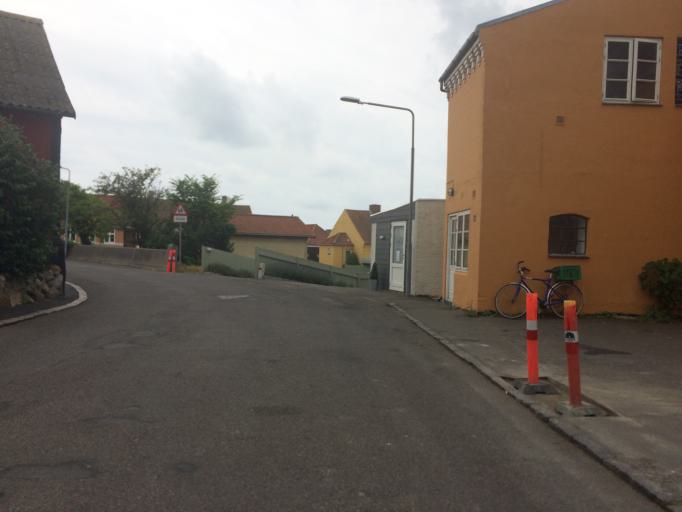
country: DK
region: Capital Region
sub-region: Bornholm Kommune
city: Ronne
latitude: 55.1854
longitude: 14.7070
